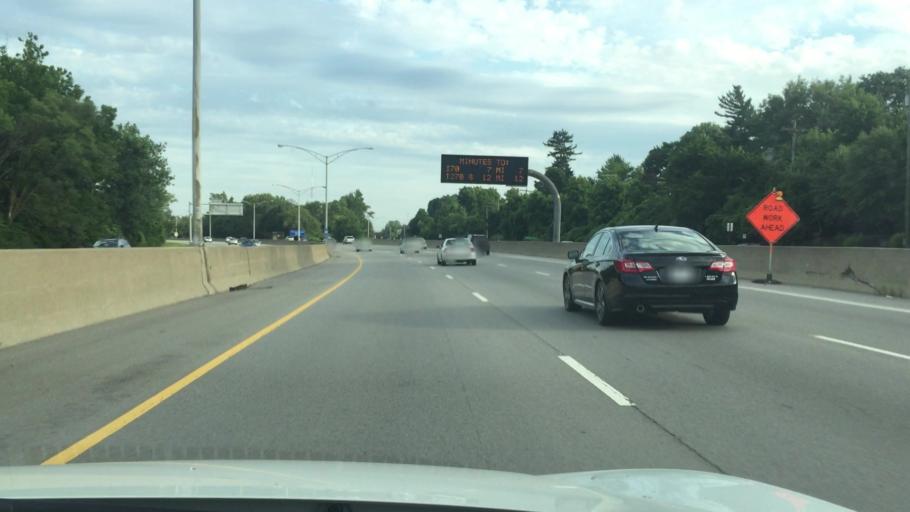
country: US
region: Ohio
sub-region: Franklin County
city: Worthington
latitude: 40.0447
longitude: -83.0334
